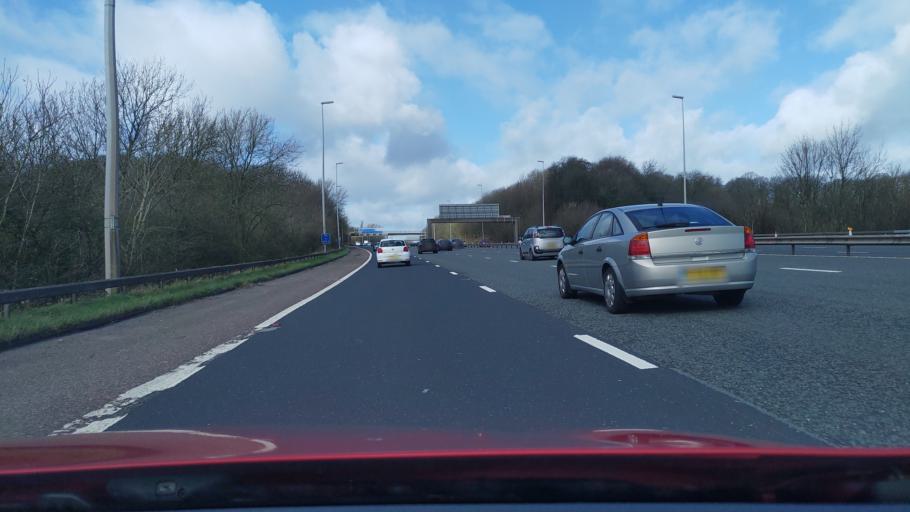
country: GB
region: England
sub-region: Lancashire
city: Goosnargh
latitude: 53.7731
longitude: -2.6407
